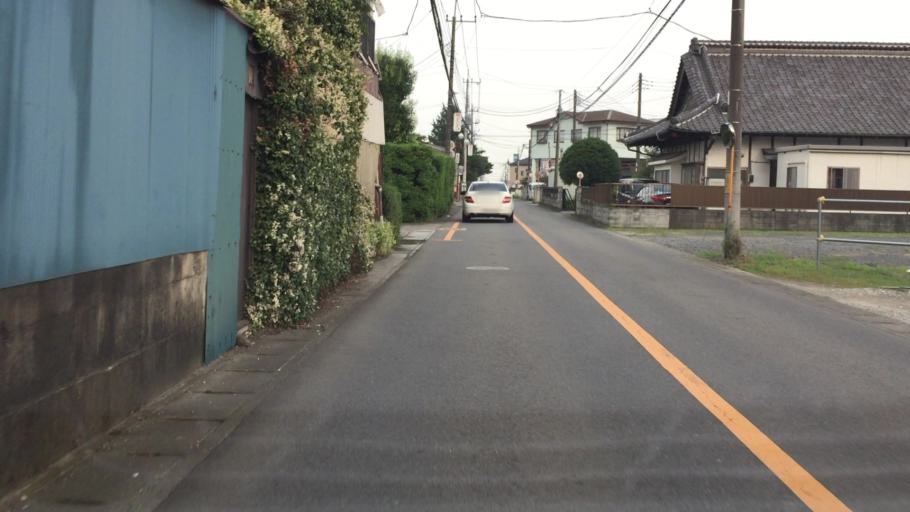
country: JP
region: Tochigi
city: Tochigi
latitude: 36.3956
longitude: 139.7186
